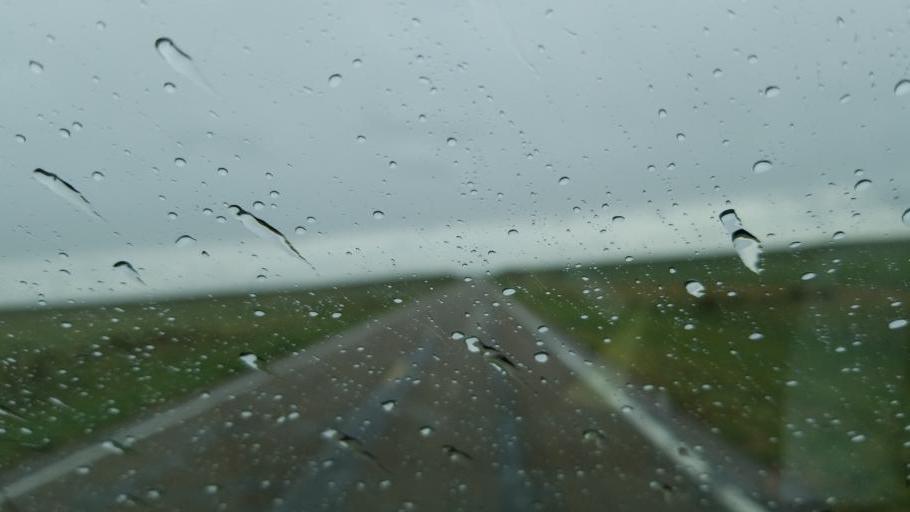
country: US
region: Colorado
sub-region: Lincoln County
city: Hugo
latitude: 38.8497
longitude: -103.1949
